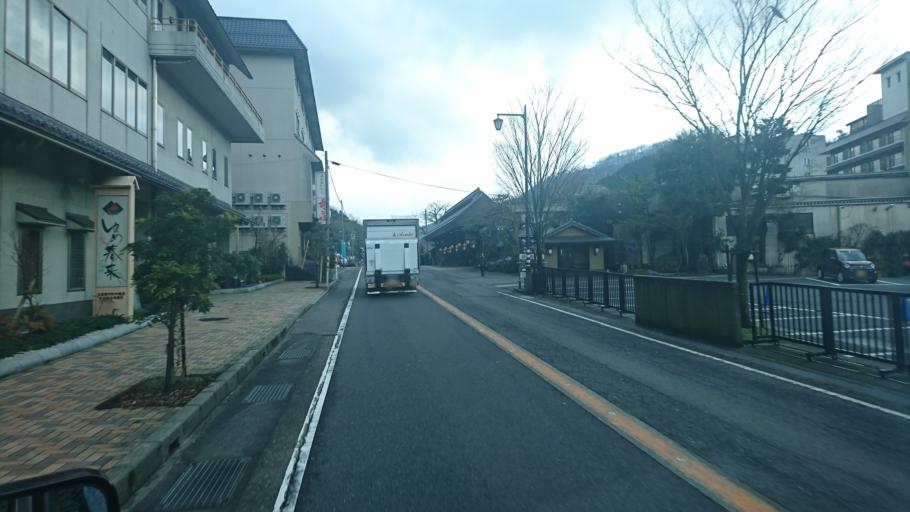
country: JP
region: Tottori
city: Tottori
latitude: 35.5567
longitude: 134.4889
